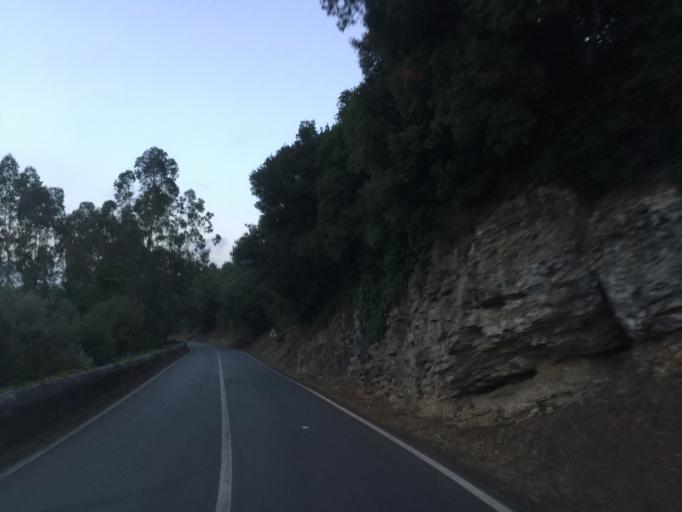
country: PT
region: Leiria
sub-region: Bombarral
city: Bombarral
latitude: 39.2957
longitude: -9.2004
